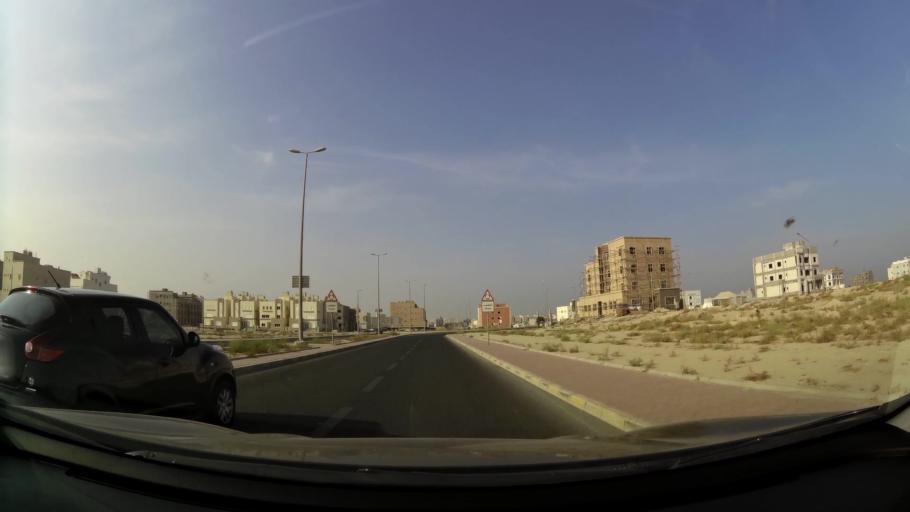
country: KW
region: Mubarak al Kabir
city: Mubarak al Kabir
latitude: 29.2018
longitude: 48.1011
